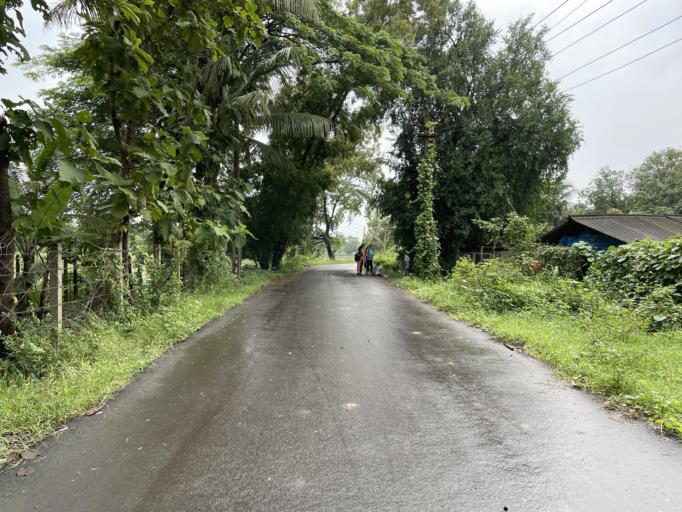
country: IN
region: Gujarat
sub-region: Valsad
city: Pardi
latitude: 20.4571
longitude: 72.9332
